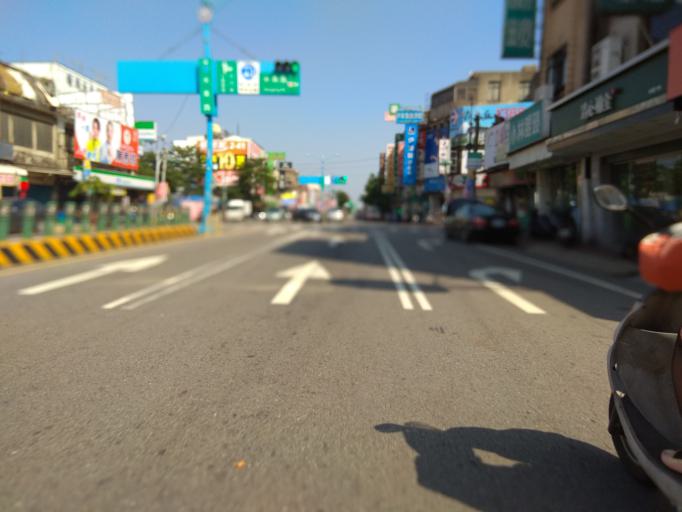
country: TW
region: Taiwan
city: Daxi
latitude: 24.9189
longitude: 121.1836
